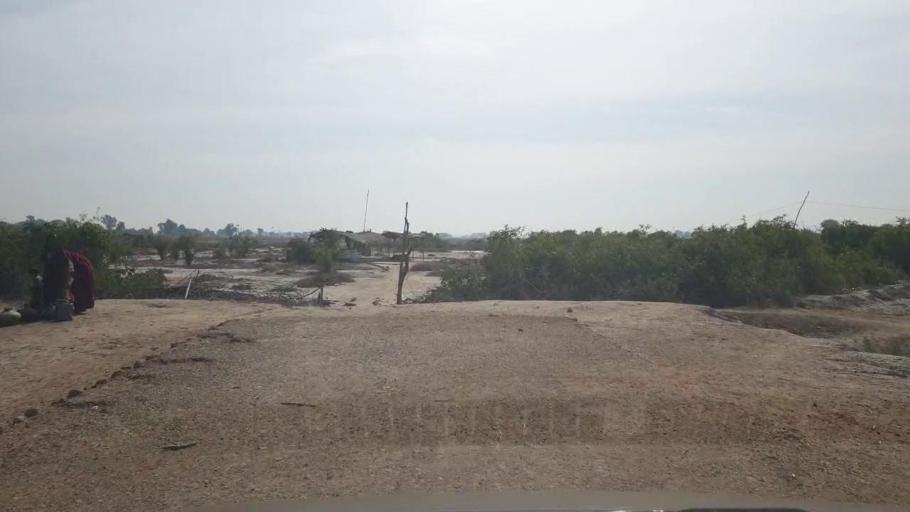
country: PK
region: Sindh
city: Umarkot
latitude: 25.3573
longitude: 69.6556
